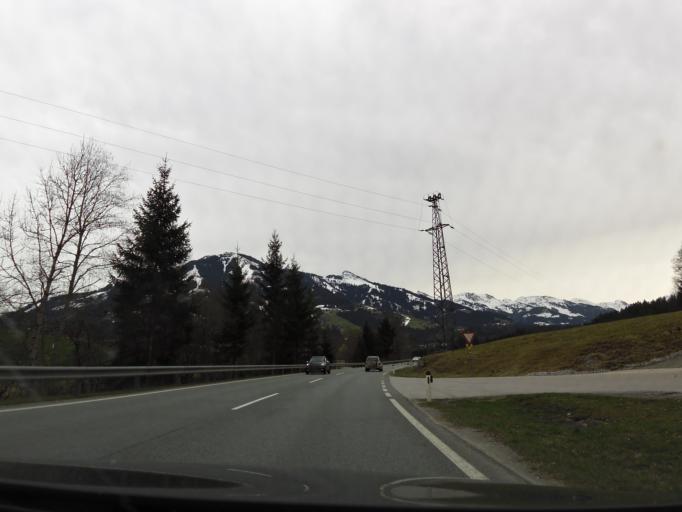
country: AT
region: Tyrol
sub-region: Politischer Bezirk Kitzbuhel
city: Westendorf
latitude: 47.4382
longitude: 12.1912
